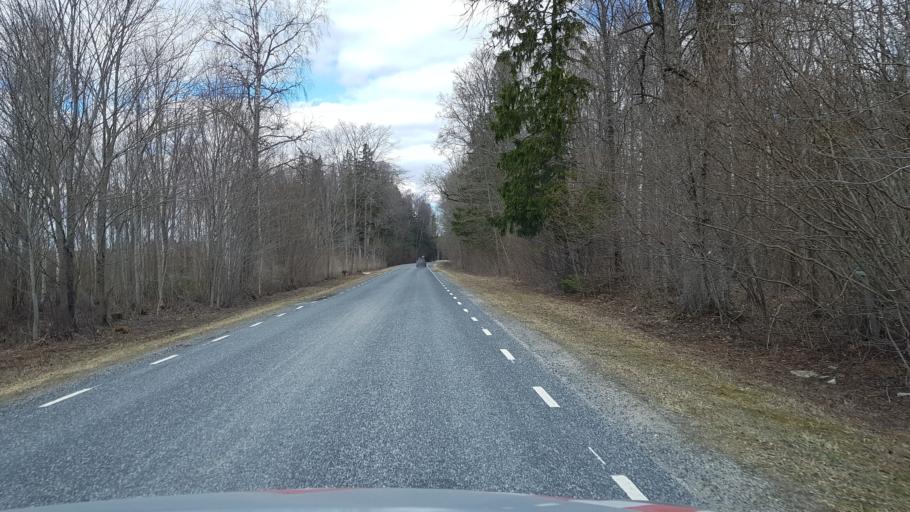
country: EE
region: Laeaene-Virumaa
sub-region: Tamsalu vald
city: Tamsalu
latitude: 59.1908
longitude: 26.1302
